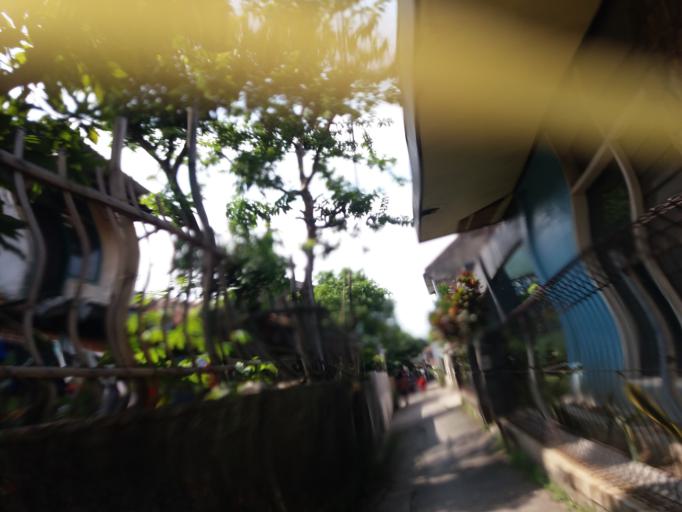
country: ID
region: West Java
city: Bandung
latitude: -6.9187
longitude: 107.6486
